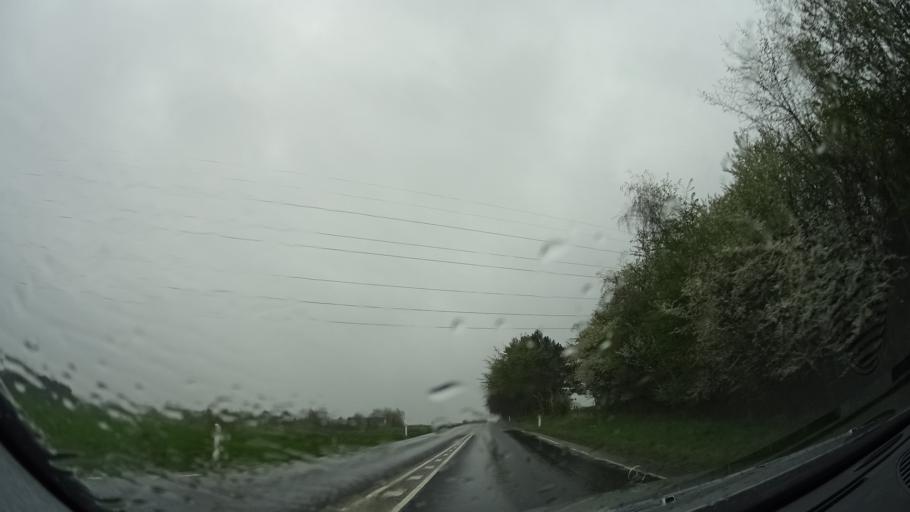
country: DK
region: Zealand
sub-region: Odsherred Kommune
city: Asnaes
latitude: 55.8287
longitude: 11.5722
